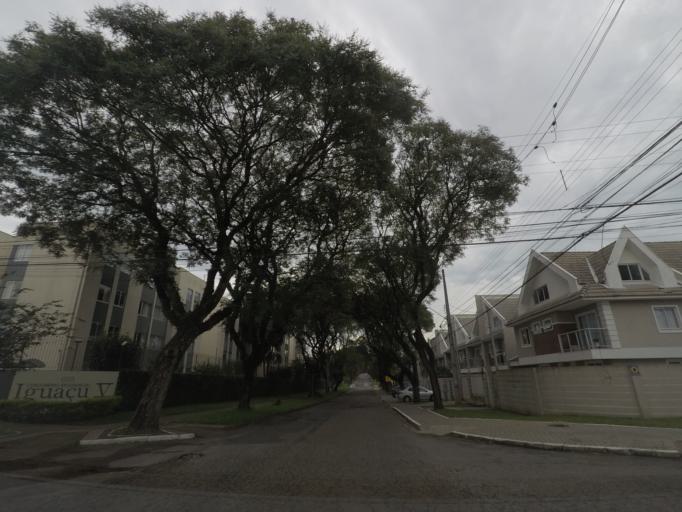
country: BR
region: Parana
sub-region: Curitiba
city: Curitiba
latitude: -25.4808
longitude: -49.3014
